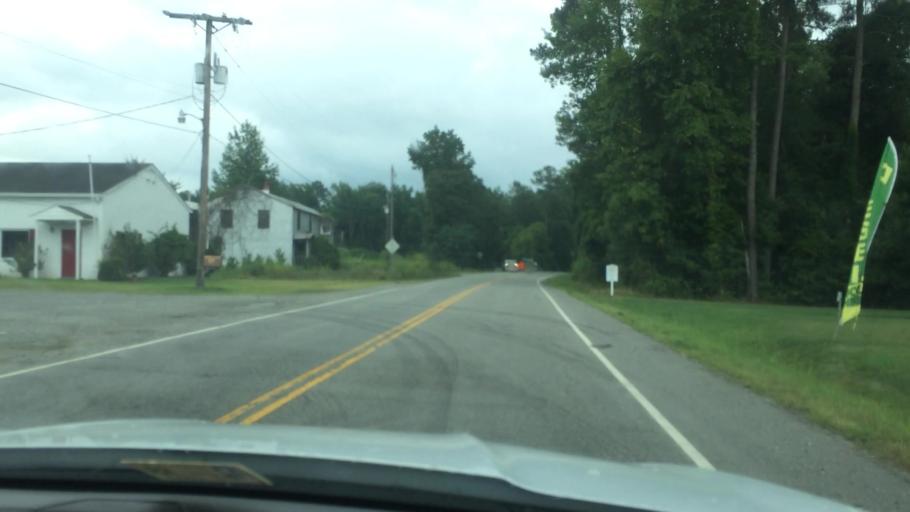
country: US
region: Virginia
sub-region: New Kent County
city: New Kent
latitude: 37.4406
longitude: -77.0409
